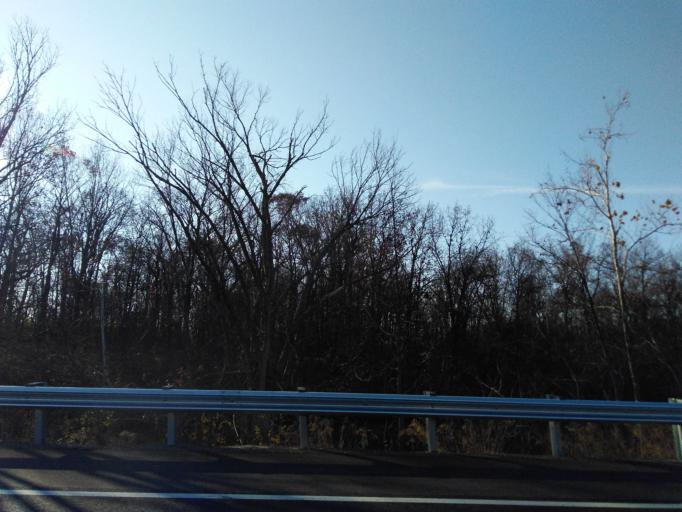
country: US
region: Illinois
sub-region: Madison County
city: Highland
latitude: 38.7861
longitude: -89.6992
